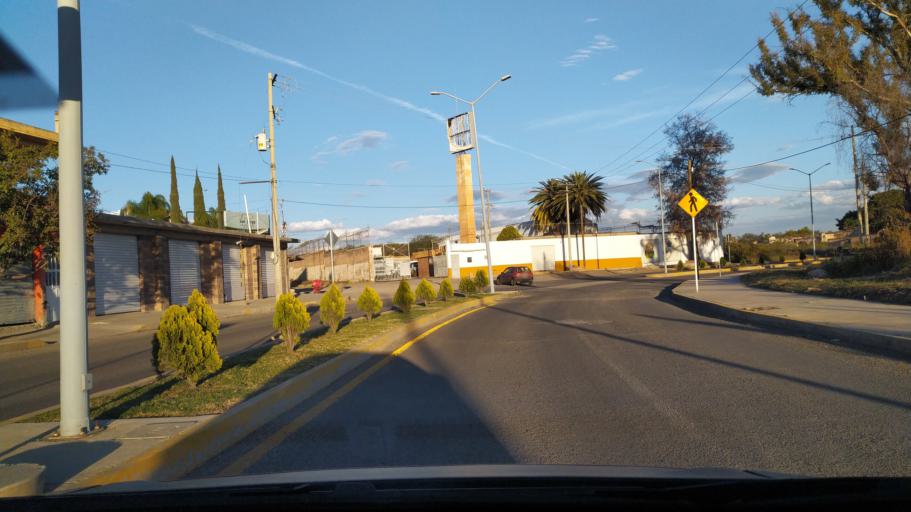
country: MX
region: Guanajuato
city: Ciudad Manuel Doblado
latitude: 20.7347
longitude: -101.9491
